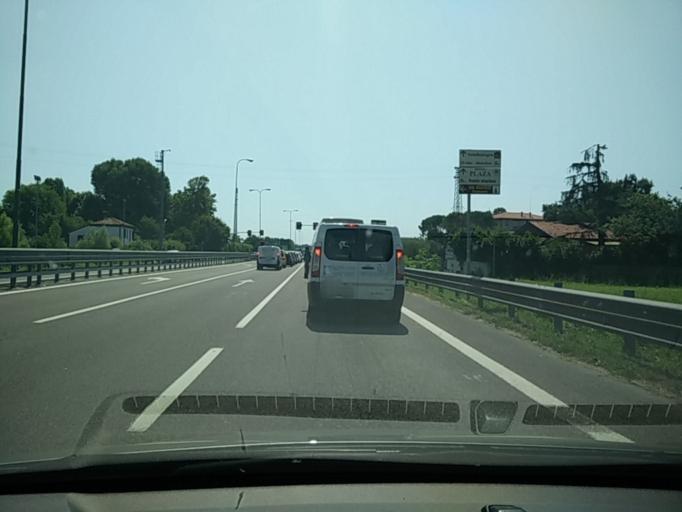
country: IT
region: Veneto
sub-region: Provincia di Venezia
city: Campalto
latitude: 45.5107
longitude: 12.2618
